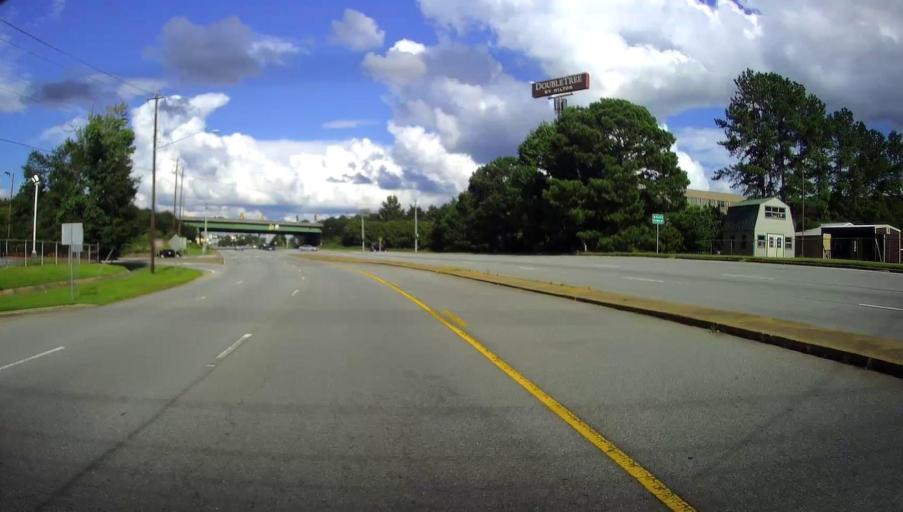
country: US
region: Alabama
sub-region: Russell County
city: Phenix City
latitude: 32.5191
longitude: -84.9555
